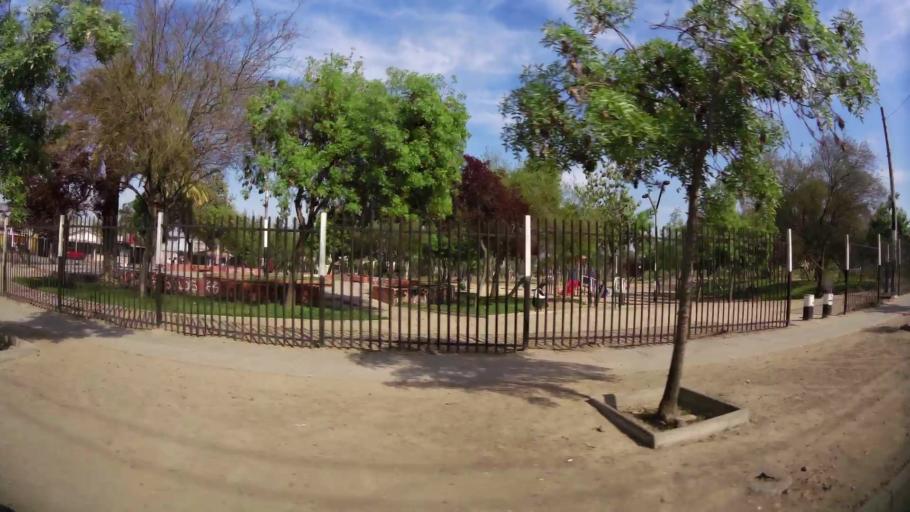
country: CL
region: Santiago Metropolitan
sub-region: Provincia de Santiago
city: Lo Prado
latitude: -33.4478
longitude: -70.7443
